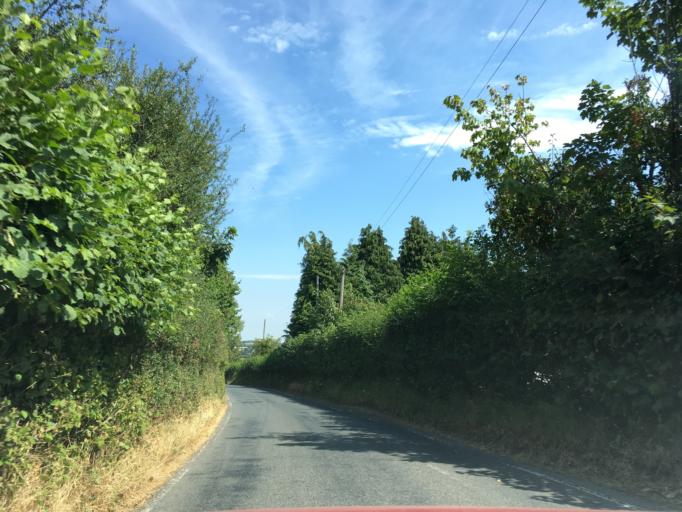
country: GB
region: Wales
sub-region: Newport
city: Langstone
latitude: 51.6125
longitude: -2.9021
